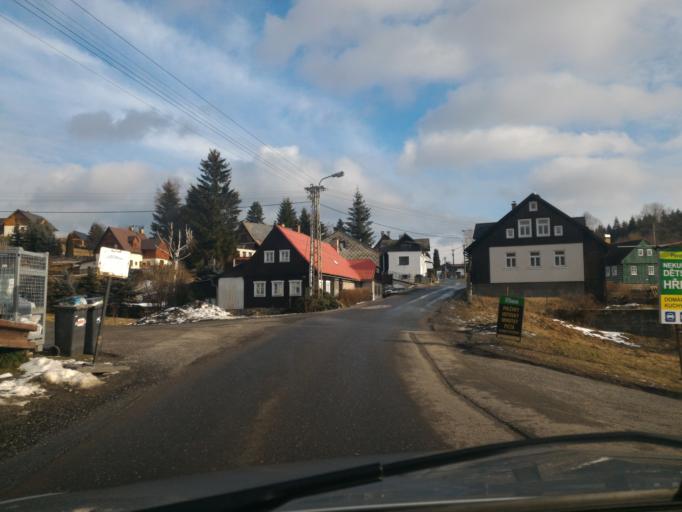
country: CZ
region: Liberecky
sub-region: Okres Jablonec nad Nisou
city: Desna
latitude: 50.7596
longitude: 15.2891
